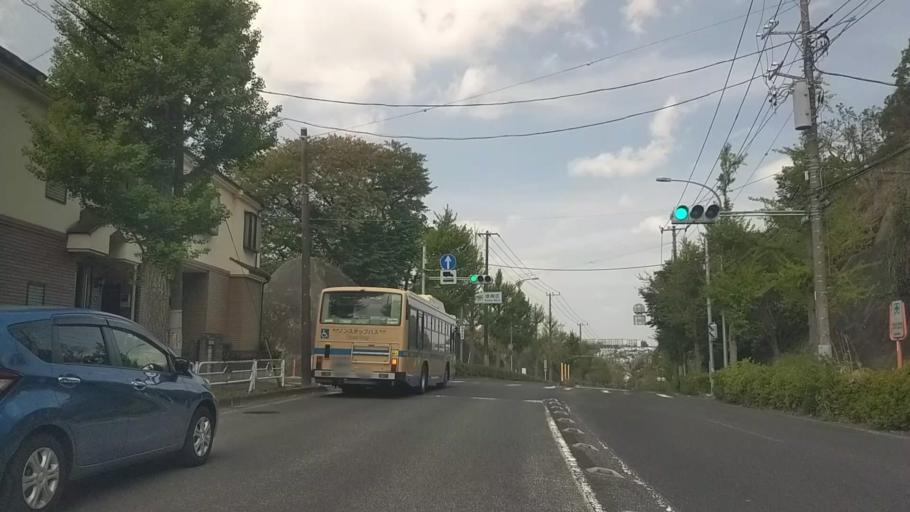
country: JP
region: Kanagawa
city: Yokohama
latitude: 35.3865
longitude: 139.5888
